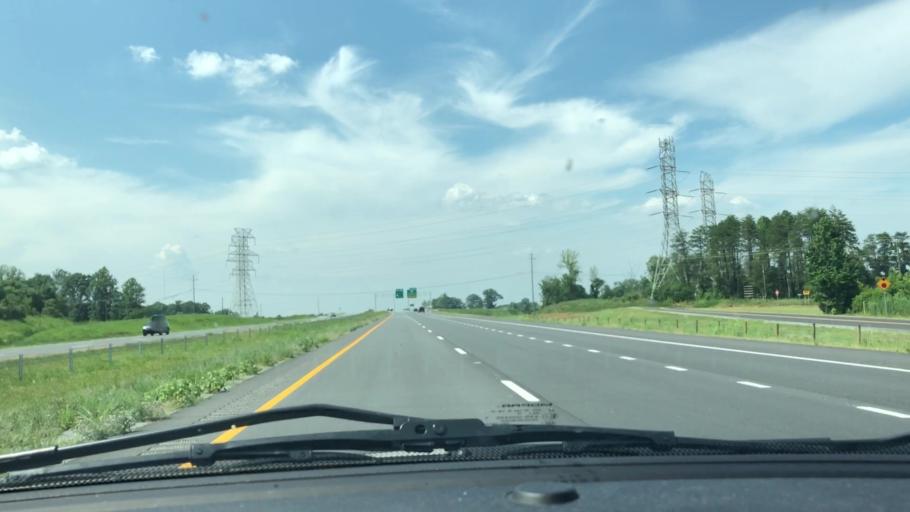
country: US
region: North Carolina
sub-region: Guilford County
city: Summerfield
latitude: 36.2401
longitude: -79.9189
